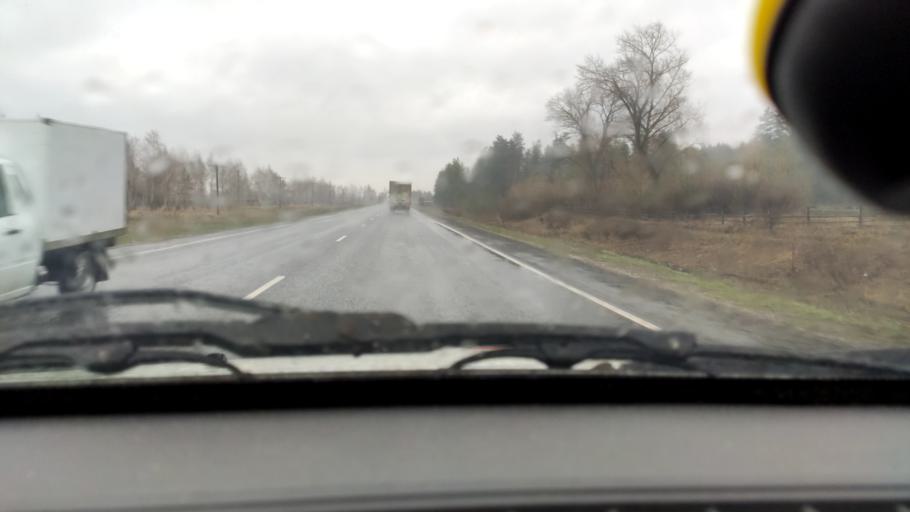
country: RU
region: Samara
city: Povolzhskiy
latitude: 53.5977
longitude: 49.5900
